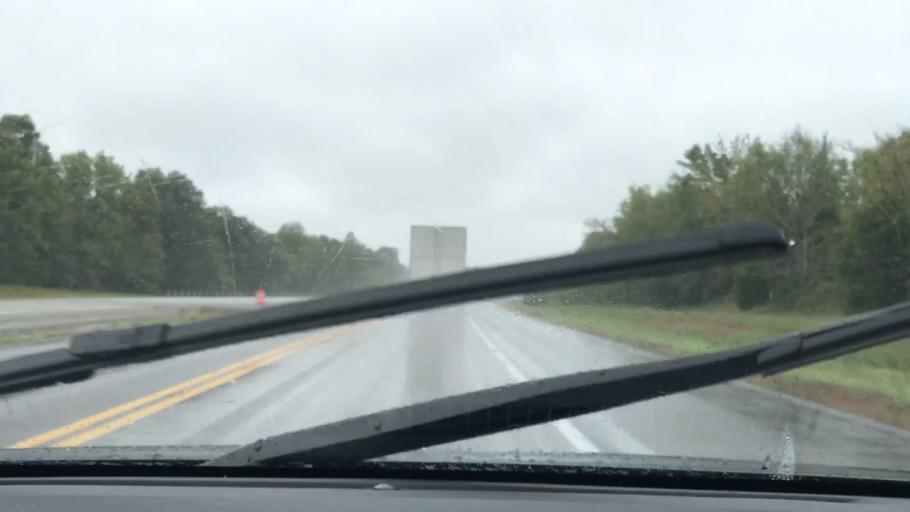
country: US
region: Kentucky
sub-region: Christian County
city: Hopkinsville
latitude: 37.0134
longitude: -87.4574
